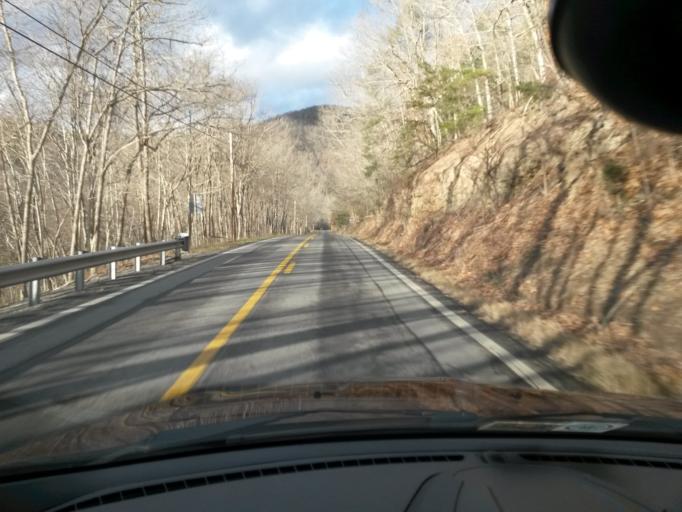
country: US
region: West Virginia
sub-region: Monroe County
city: Union
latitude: 37.5202
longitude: -80.6169
